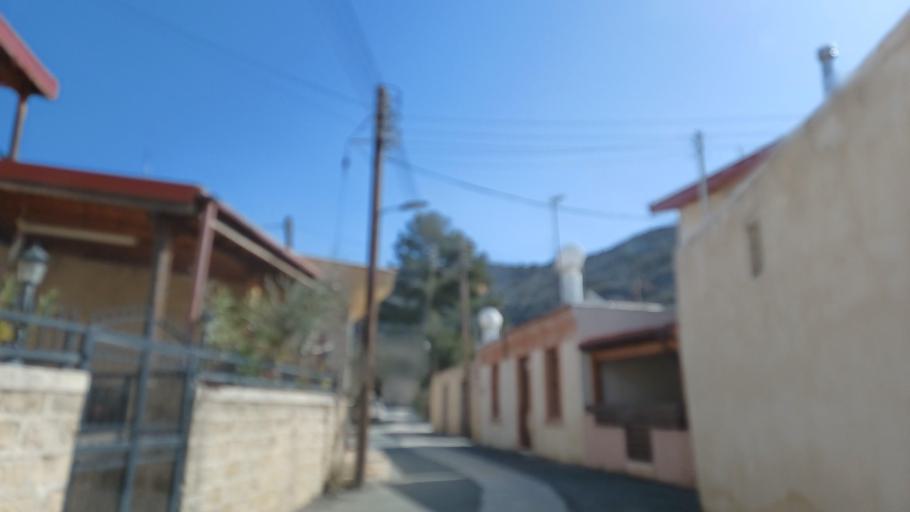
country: CY
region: Limassol
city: Pachna
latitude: 34.8488
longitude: 32.7462
